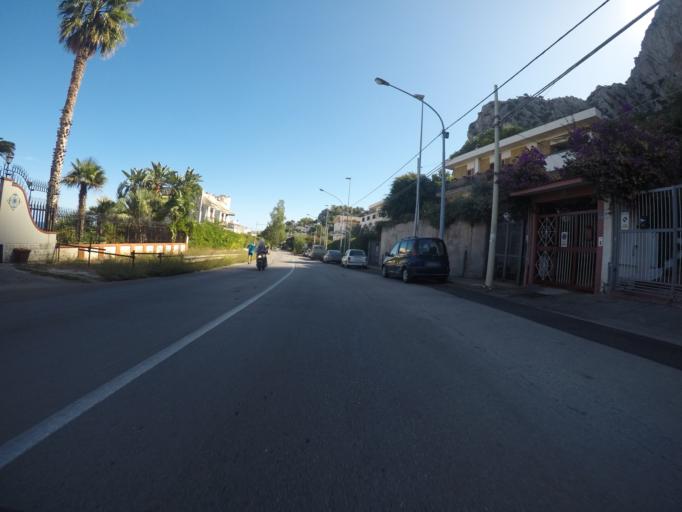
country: IT
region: Sicily
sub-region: Palermo
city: Palermo
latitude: 38.1887
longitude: 13.3523
